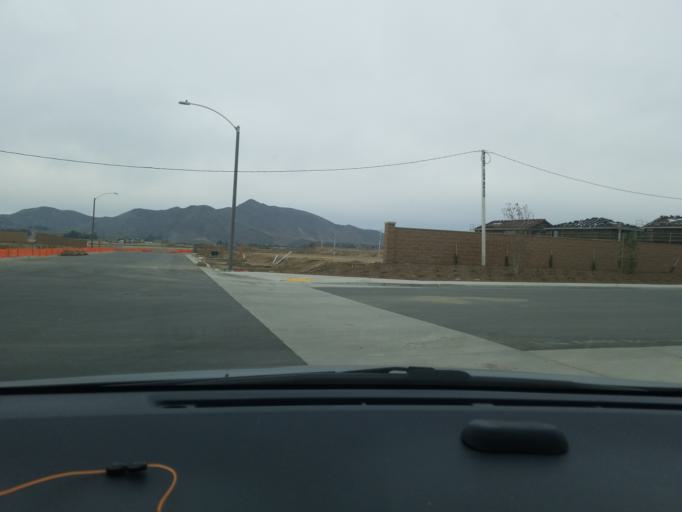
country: US
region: California
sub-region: Riverside County
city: Winchester
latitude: 33.6943
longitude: -117.0980
